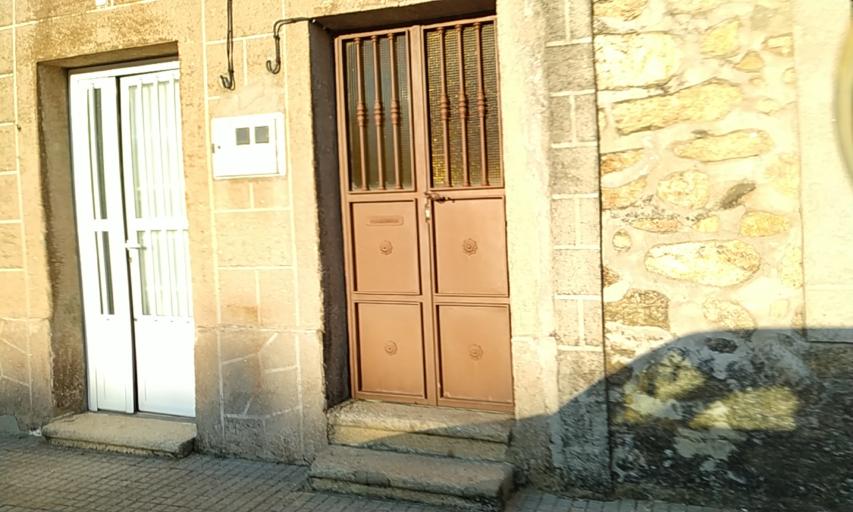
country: PT
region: Portalegre
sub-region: Portalegre
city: Sao Juliao
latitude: 39.3486
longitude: -7.2753
